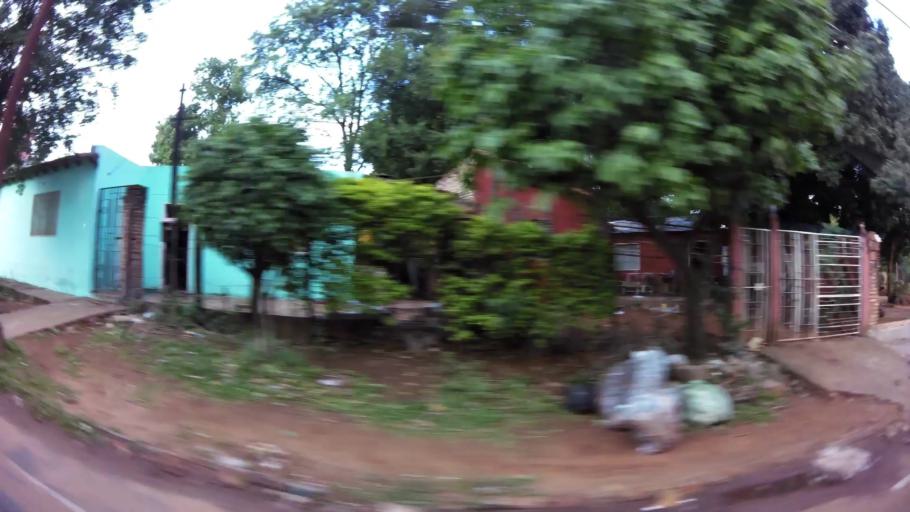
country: PY
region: Central
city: Fernando de la Mora
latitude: -25.3612
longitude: -57.5422
